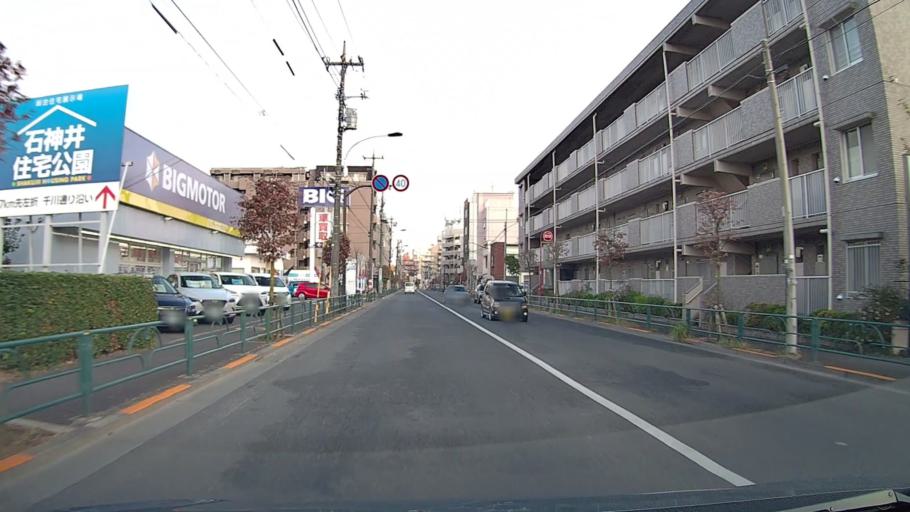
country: JP
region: Tokyo
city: Musashino
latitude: 35.7315
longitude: 139.5690
